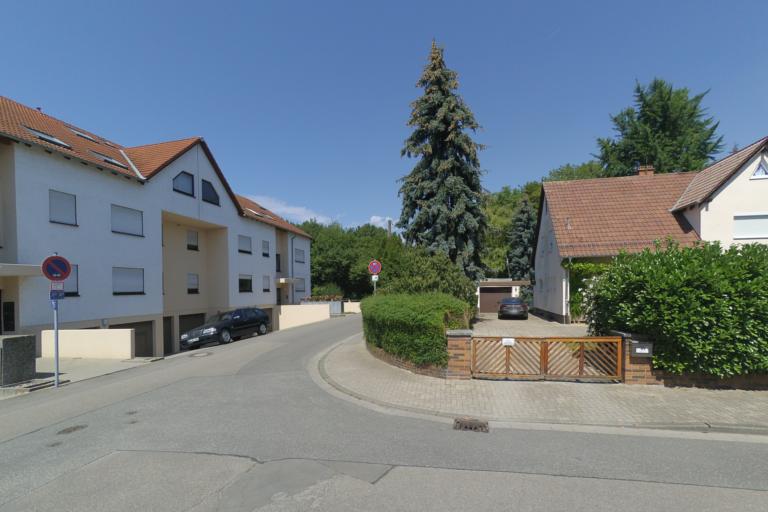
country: DE
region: Rheinland-Pfalz
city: Altrip
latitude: 49.4361
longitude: 8.4940
